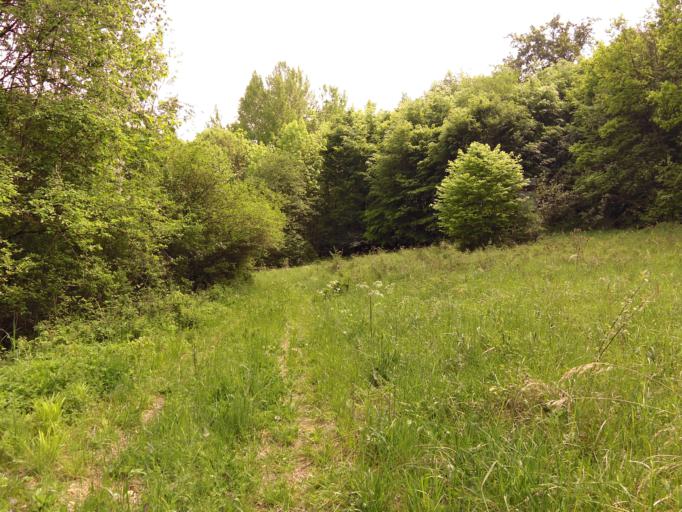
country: DE
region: Thuringia
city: Ifta
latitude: 51.0559
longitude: 10.1474
